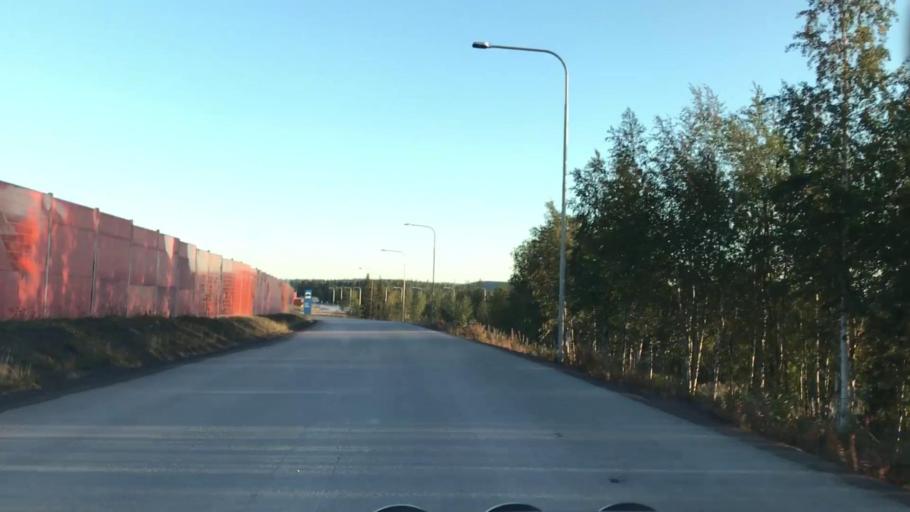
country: SE
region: Norrbotten
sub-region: Gallivare Kommun
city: Malmberget
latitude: 67.6502
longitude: 21.0184
